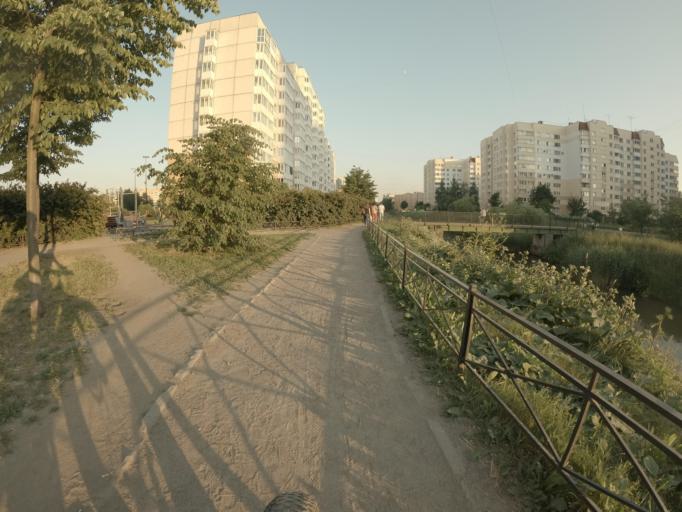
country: RU
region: St.-Petersburg
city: Dachnoye
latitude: 59.8506
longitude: 30.2466
